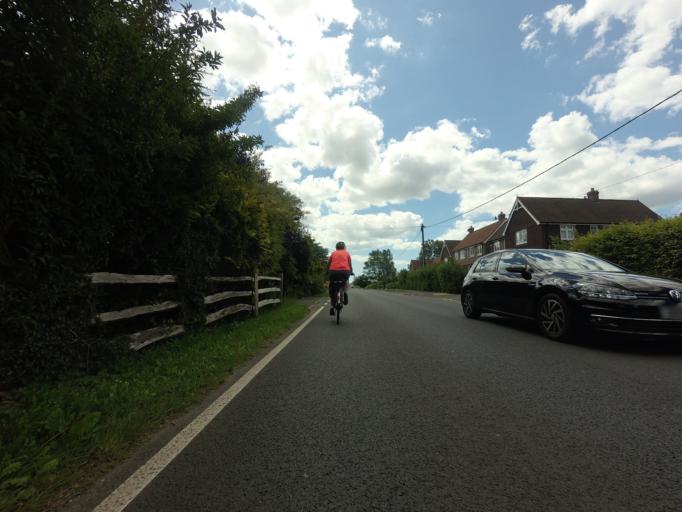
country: GB
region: England
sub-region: East Sussex
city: Seaford
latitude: 50.8389
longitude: 0.1657
